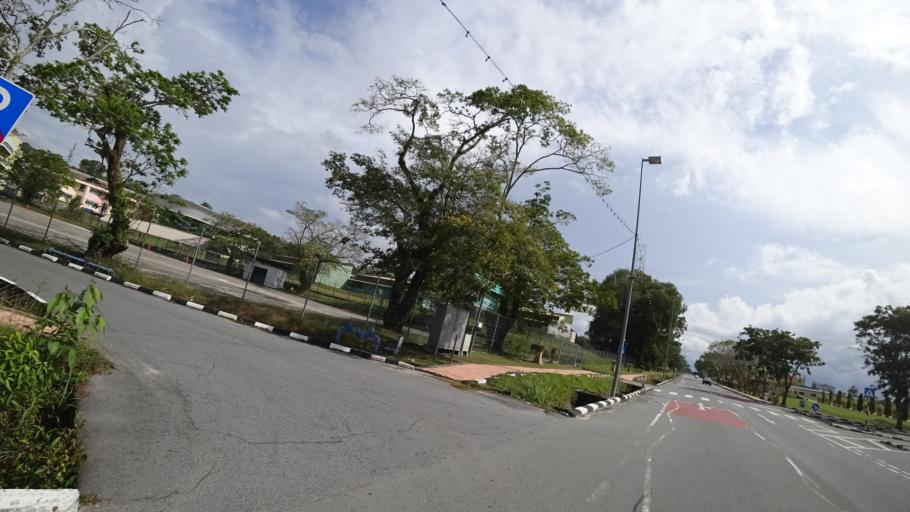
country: BN
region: Tutong
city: Tutong
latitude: 4.8141
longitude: 114.6629
